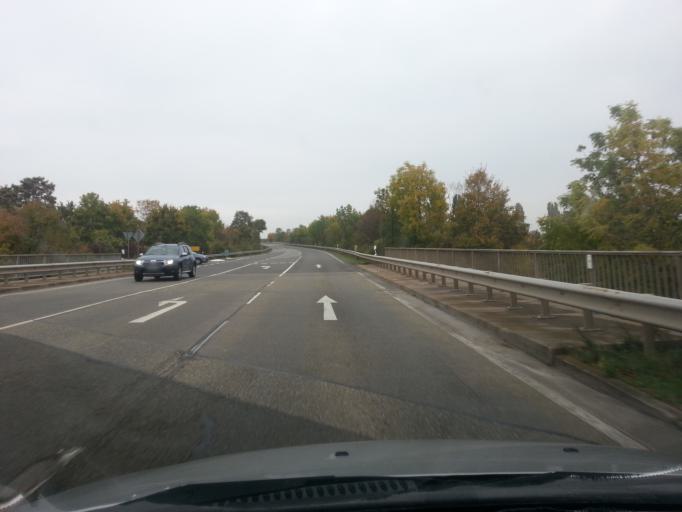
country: DE
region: Rheinland-Pfalz
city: Walsheim
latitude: 49.2350
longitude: 8.1303
